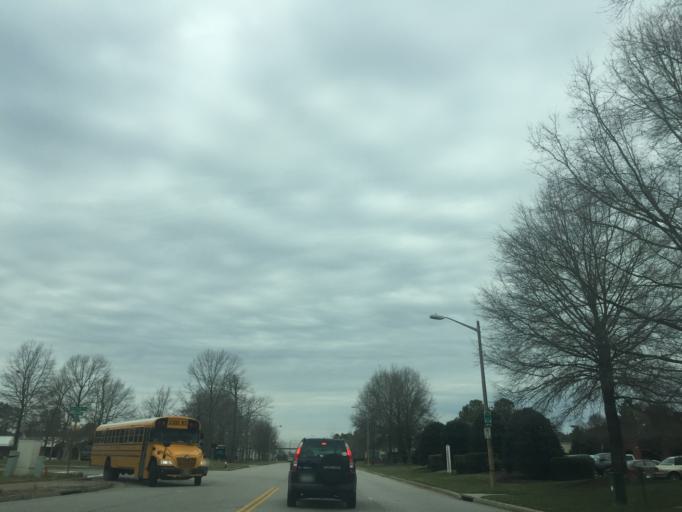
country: US
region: Virginia
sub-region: City of Newport News
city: Newport News
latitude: 37.0948
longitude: -76.4673
